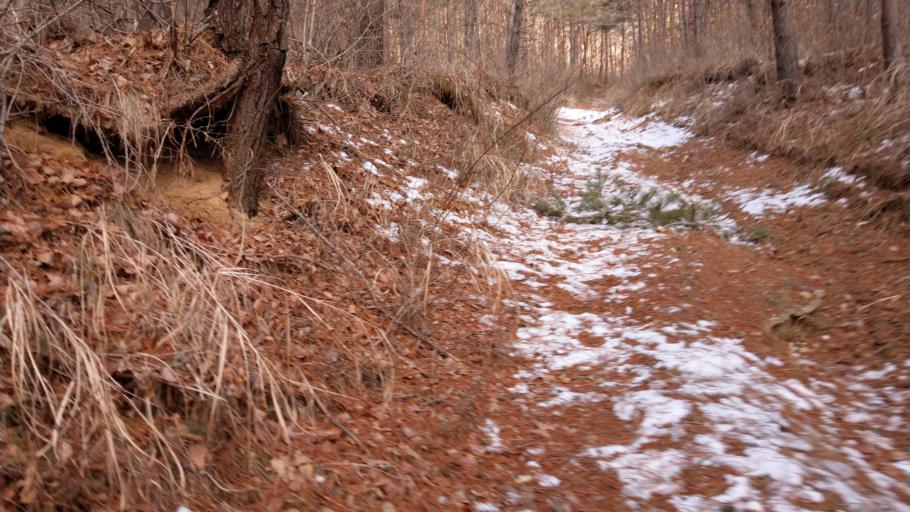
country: JP
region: Nagano
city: Komoro
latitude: 36.3659
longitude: 138.4330
